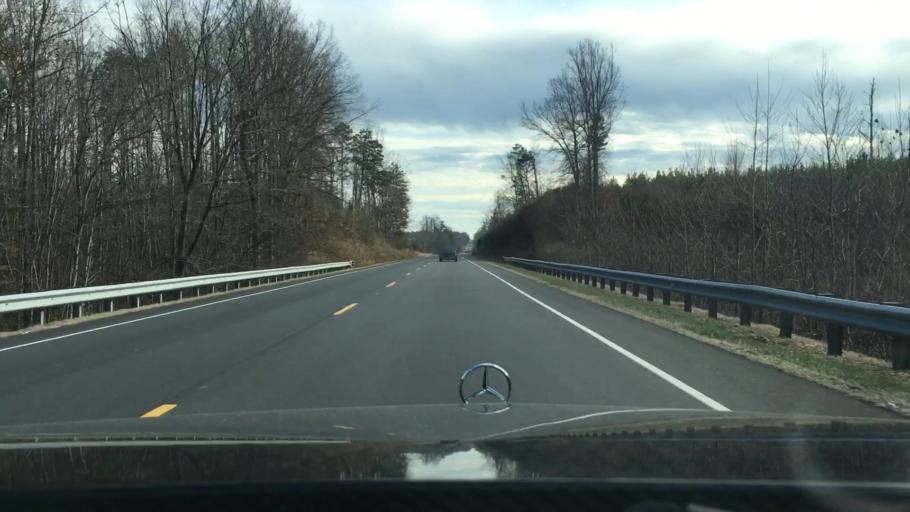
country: US
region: Virginia
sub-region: City of Danville
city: Danville
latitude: 36.5168
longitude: -79.3935
